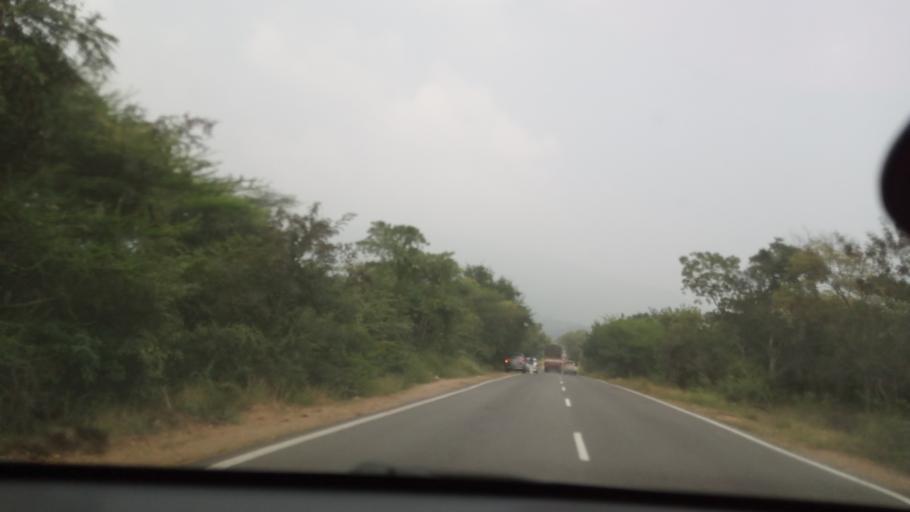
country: IN
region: Tamil Nadu
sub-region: Erode
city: Sathyamangalam
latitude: 11.5717
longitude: 77.1344
